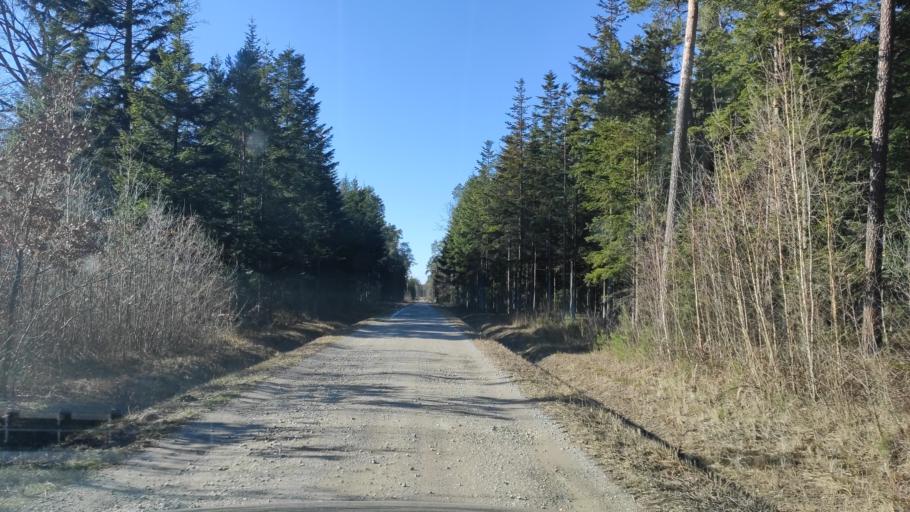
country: PL
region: Masovian Voivodeship
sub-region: Powiat radomski
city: Jedlnia-Letnisko
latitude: 51.4682
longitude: 21.3102
